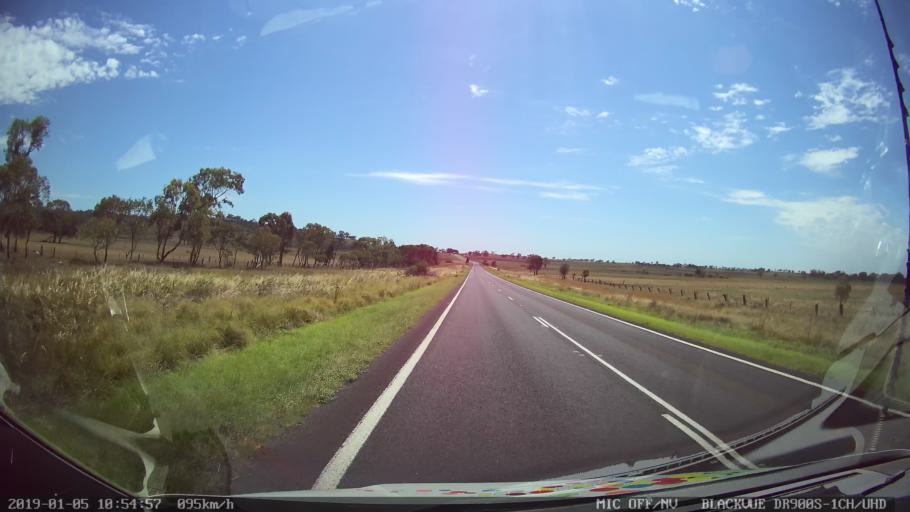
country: AU
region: New South Wales
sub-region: Warrumbungle Shire
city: Coonabarabran
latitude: -31.4504
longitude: 149.1358
